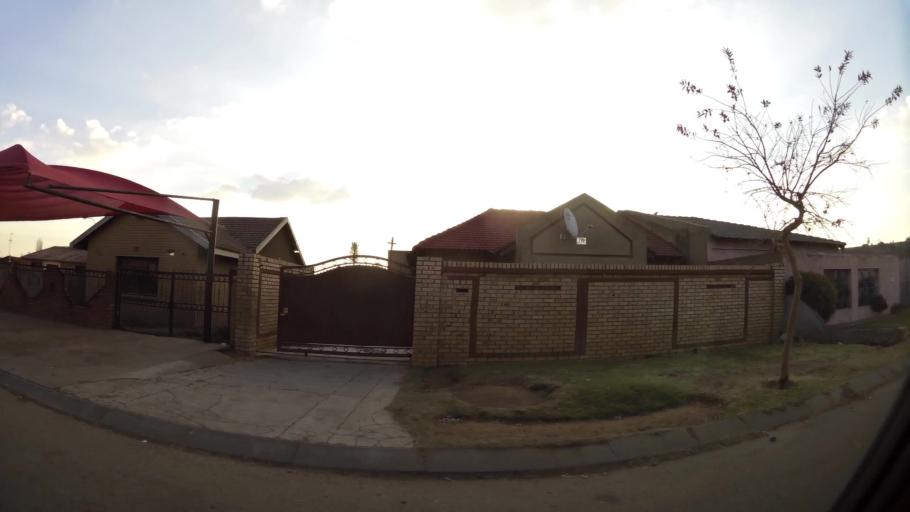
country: ZA
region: Gauteng
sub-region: City of Johannesburg Metropolitan Municipality
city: Roodepoort
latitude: -26.2093
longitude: 27.8959
